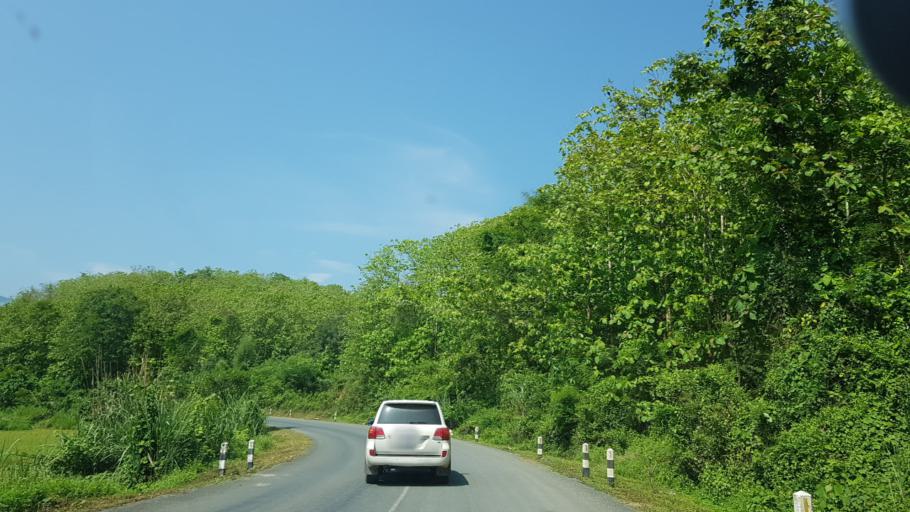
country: LA
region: Louangphabang
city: Xiang Ngeun
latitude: 19.7282
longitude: 102.1525
